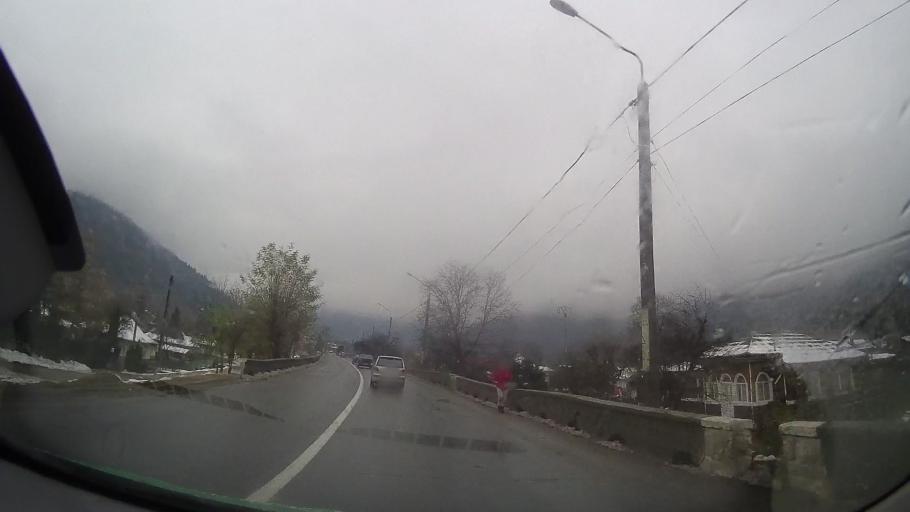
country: RO
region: Neamt
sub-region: Comuna Bicaz
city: Dodeni
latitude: 46.9061
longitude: 26.1077
